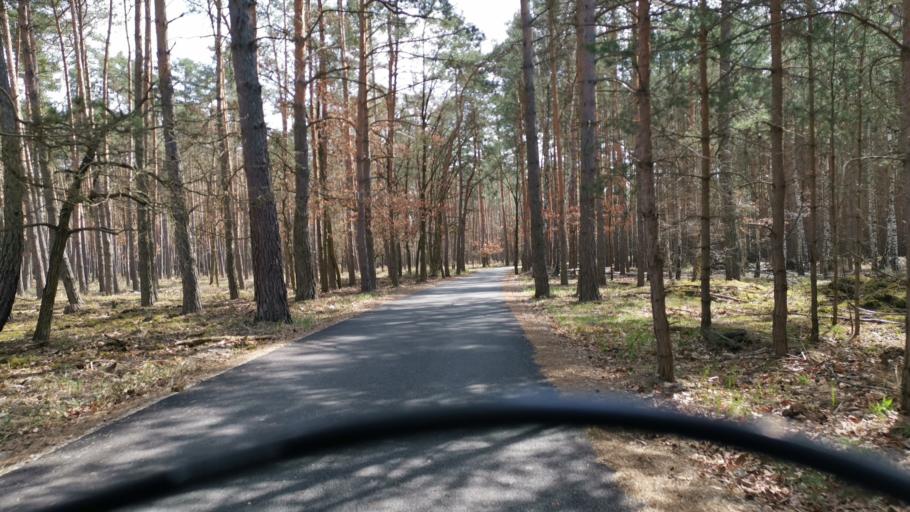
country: SK
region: Trnavsky
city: Gbely
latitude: 48.7181
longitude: 17.0522
